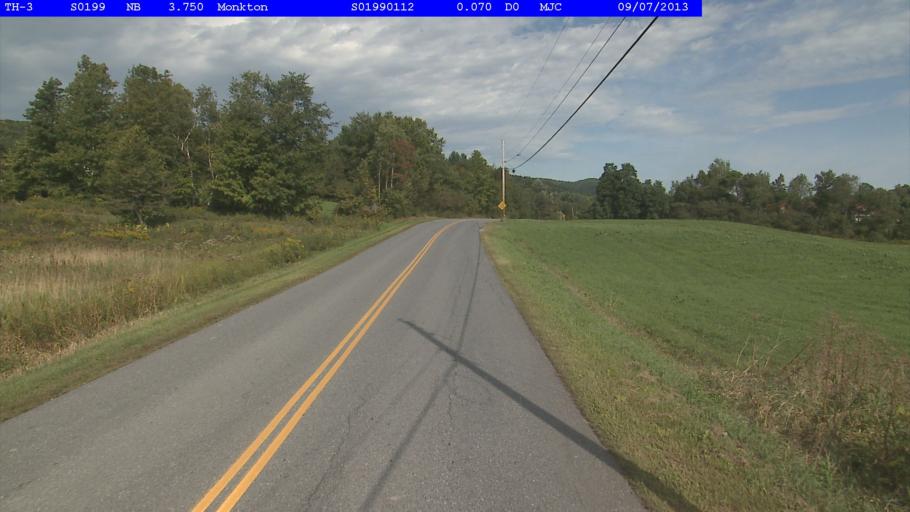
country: US
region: Vermont
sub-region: Addison County
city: Bristol
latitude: 44.1819
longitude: -73.1047
